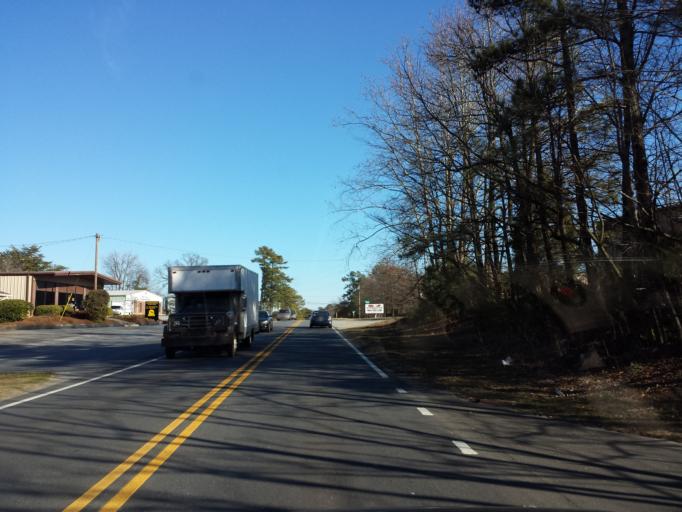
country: US
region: Georgia
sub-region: Cobb County
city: Marietta
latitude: 33.9814
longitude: -84.5675
